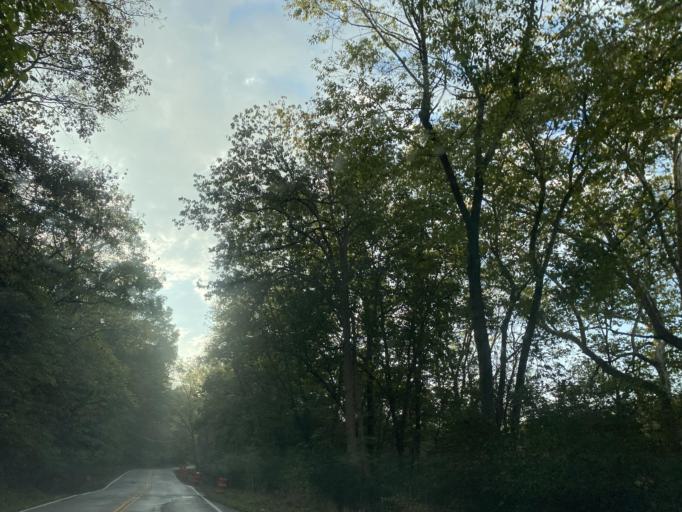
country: US
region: Kentucky
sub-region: Pendleton County
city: Falmouth
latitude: 38.7893
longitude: -84.3389
